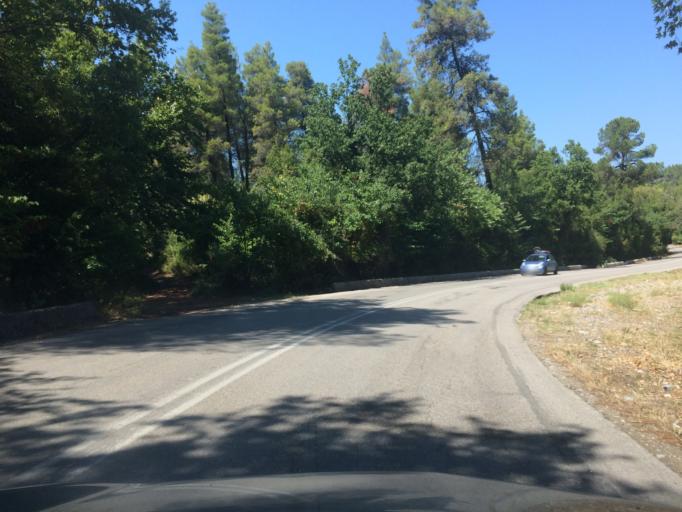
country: GR
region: Central Greece
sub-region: Nomos Evvoias
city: Prokopion
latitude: 38.7126
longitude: 23.5156
